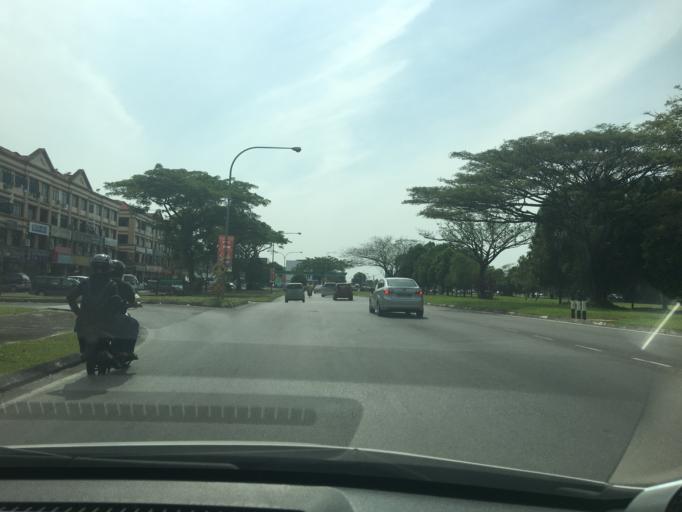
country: MY
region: Sarawak
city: Kuching
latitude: 1.5133
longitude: 110.3103
